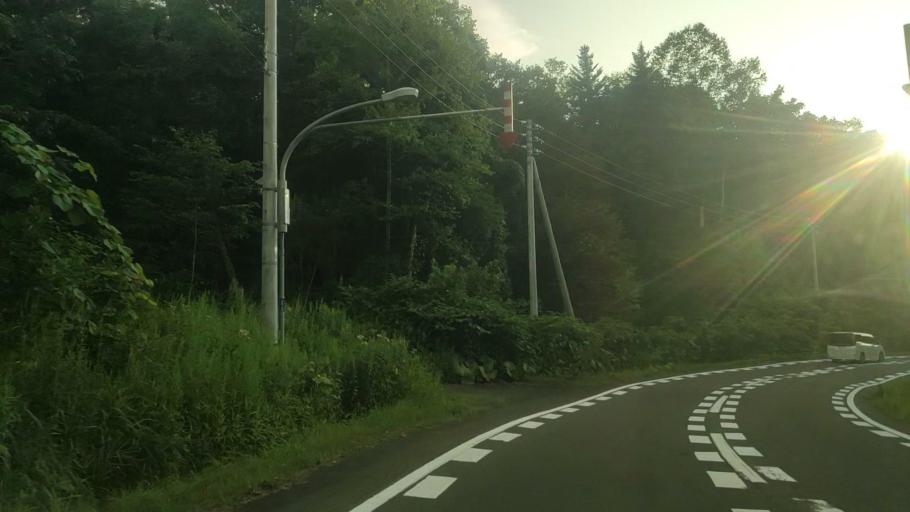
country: JP
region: Hokkaido
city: Bibai
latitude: 43.1682
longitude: 142.0738
